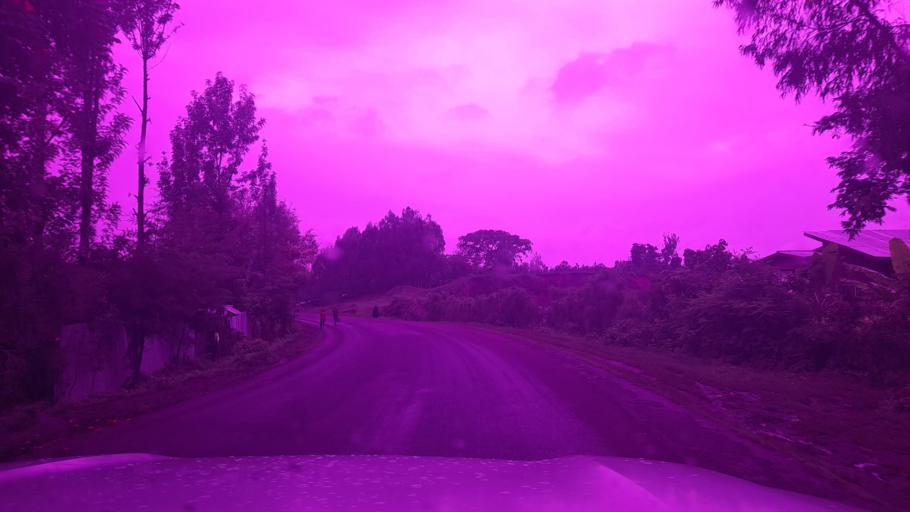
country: ET
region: Oromiya
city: Jima
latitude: 7.8365
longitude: 37.3561
